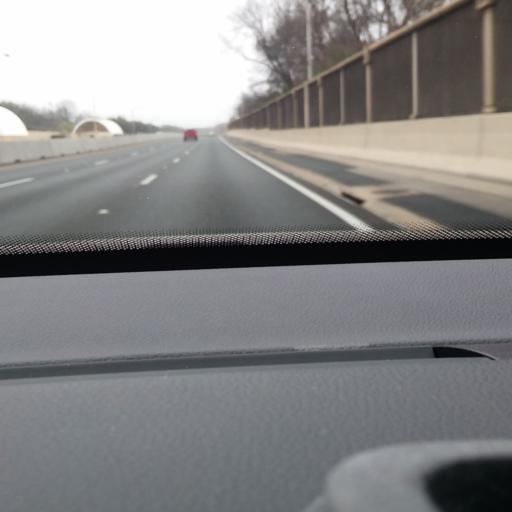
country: US
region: Texas
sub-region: Dallas County
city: Highland Park
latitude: 32.8411
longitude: -96.7847
